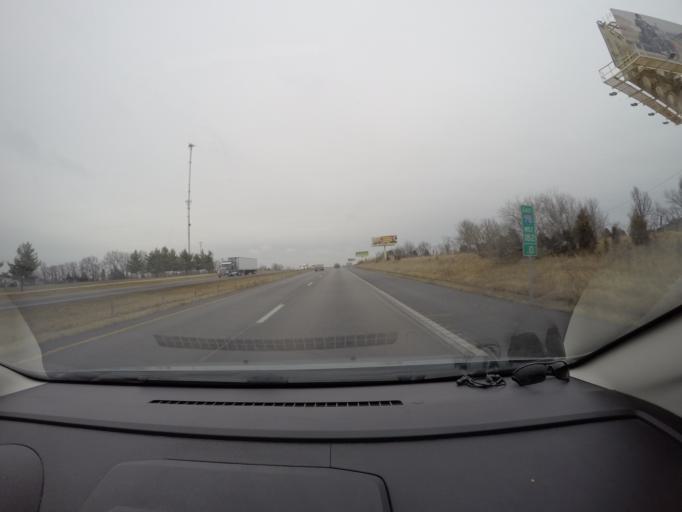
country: US
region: Missouri
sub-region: Gasconade County
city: Hermann
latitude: 38.8676
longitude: -91.3373
